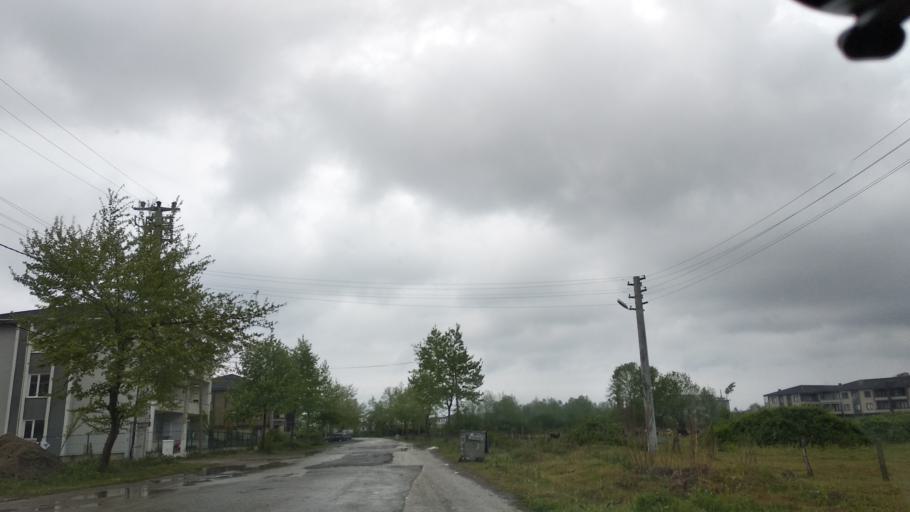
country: TR
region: Sakarya
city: Karasu
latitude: 41.0917
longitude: 30.7066
